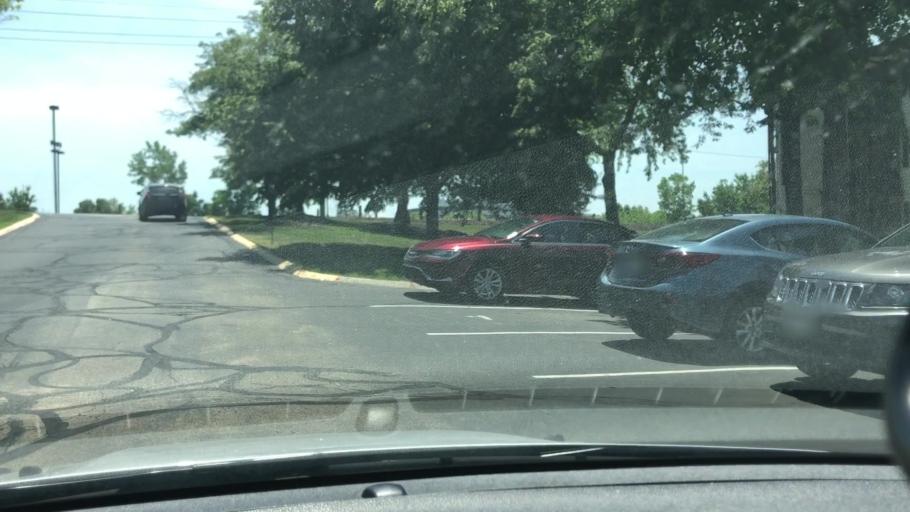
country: US
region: Indiana
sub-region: Hamilton County
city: Carmel
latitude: 39.9129
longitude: -86.0785
